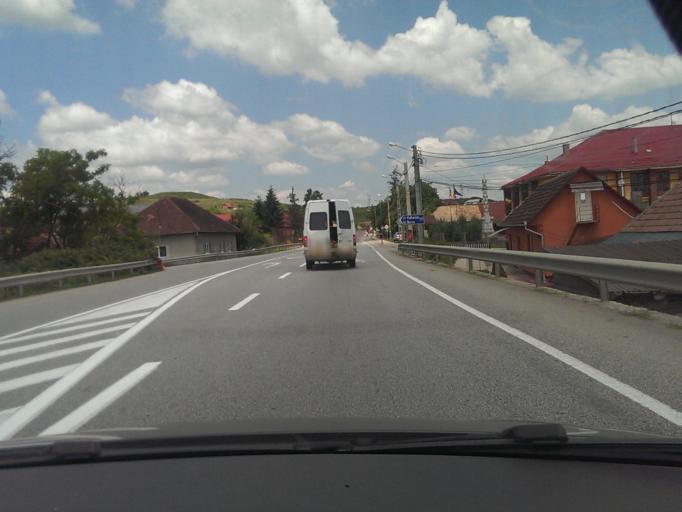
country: RO
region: Cluj
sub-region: Comuna Bontida
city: Rascruci
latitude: 46.9025
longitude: 23.7740
